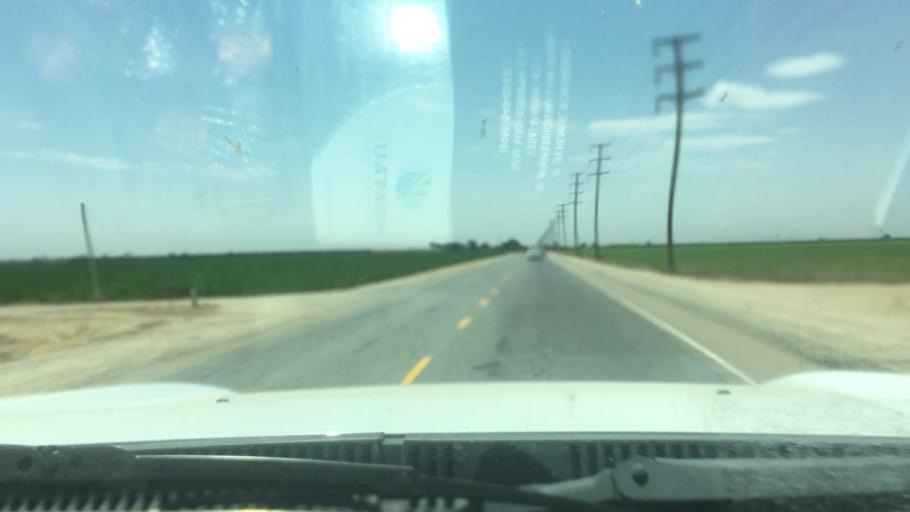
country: US
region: California
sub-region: Tulare County
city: Tipton
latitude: 36.0657
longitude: -119.2773
